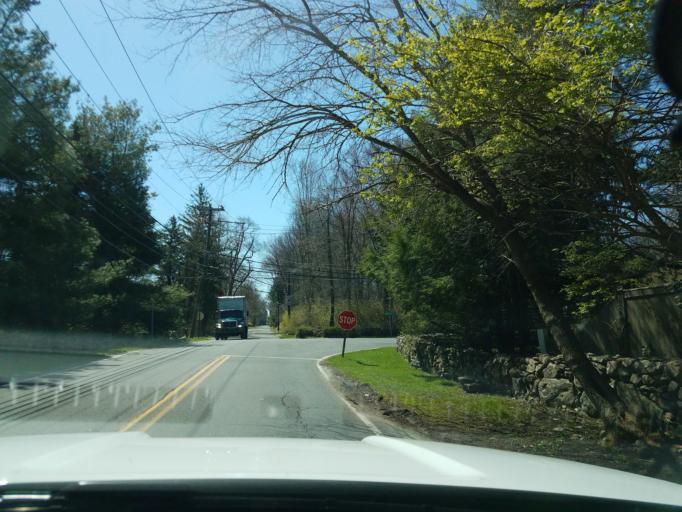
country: US
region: Connecticut
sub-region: Fairfield County
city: Westport
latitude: 41.2059
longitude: -73.3698
